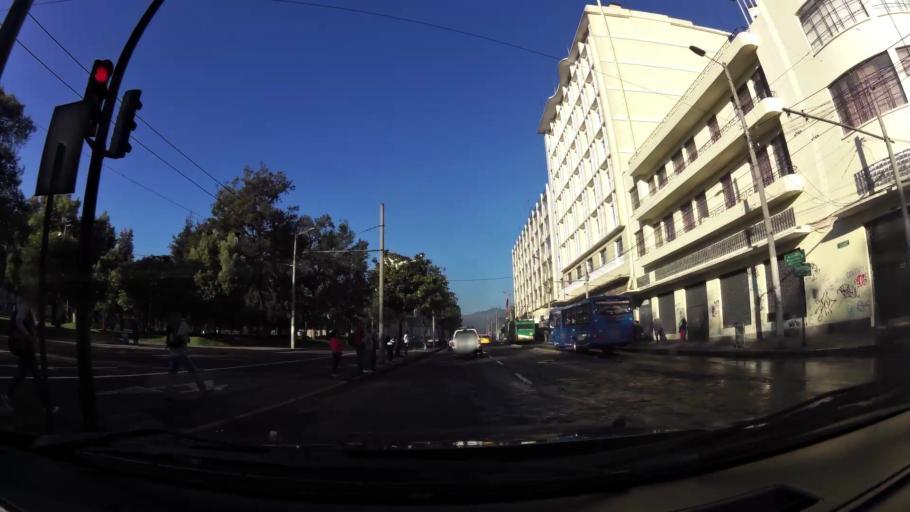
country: EC
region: Pichincha
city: Quito
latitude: -0.2148
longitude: -78.5035
